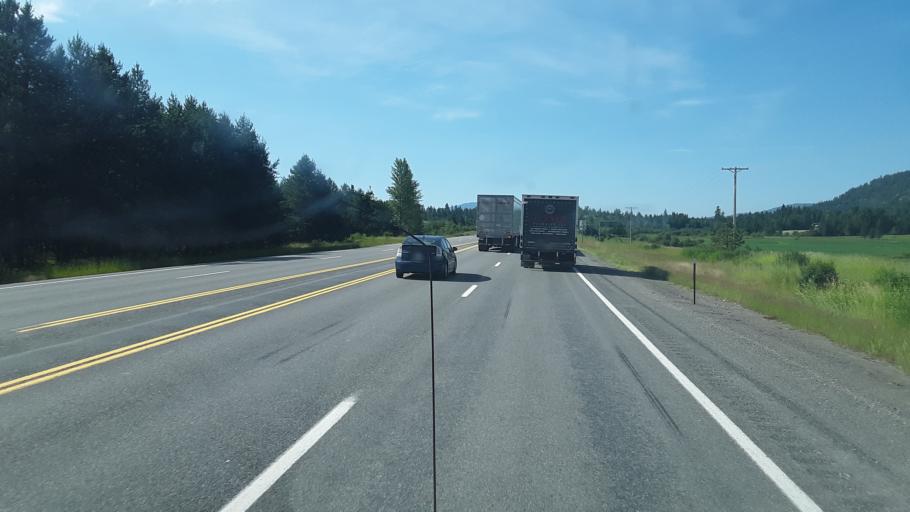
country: US
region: Idaho
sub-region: Bonner County
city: Ponderay
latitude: 48.3563
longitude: -116.5475
